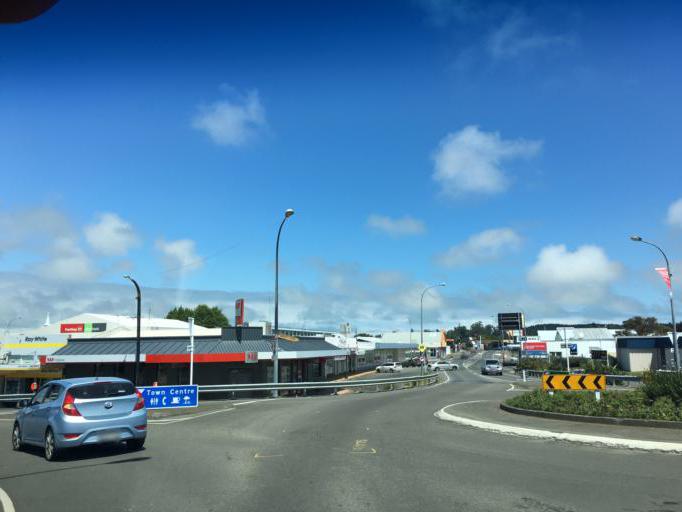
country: NZ
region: Hawke's Bay
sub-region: Wairoa District
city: Wairoa
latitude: -39.0328
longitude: 177.4185
